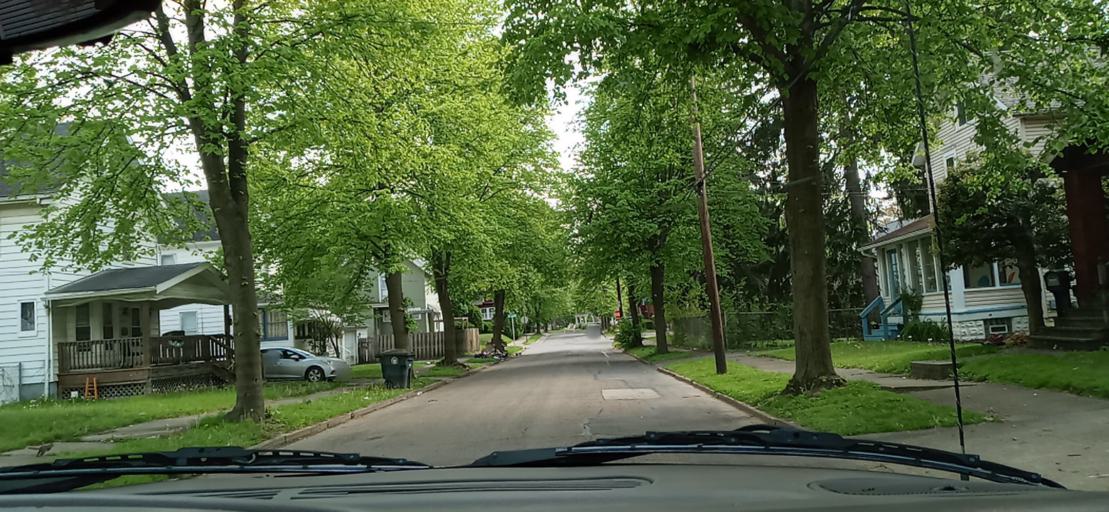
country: US
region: Ohio
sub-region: Summit County
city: Barberton
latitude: 41.0432
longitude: -81.5676
